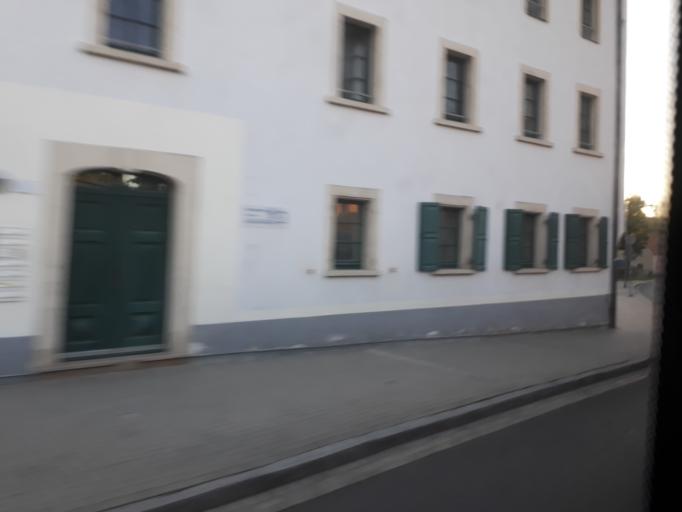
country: DE
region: Saxony
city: Radeberg
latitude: 51.0597
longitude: 13.8852
